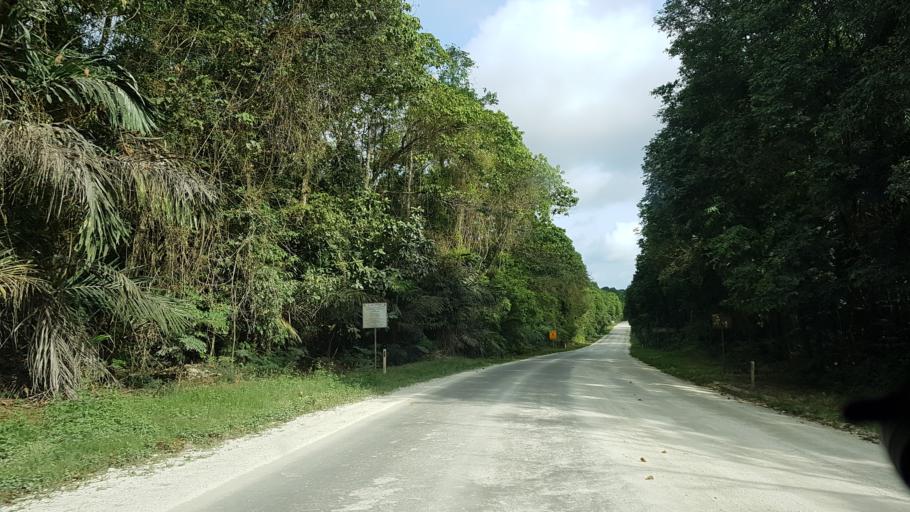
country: CX
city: Flying Fish Cove
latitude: -10.4532
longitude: 105.6879
